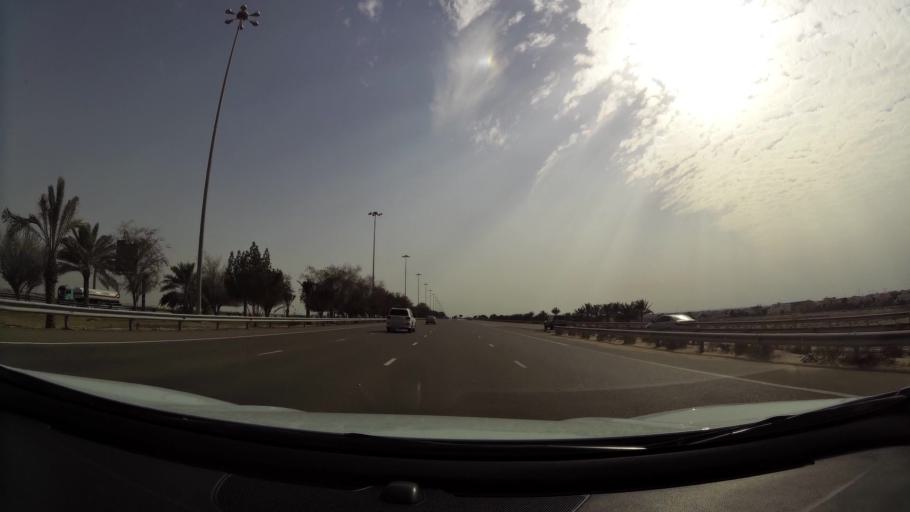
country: AE
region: Abu Dhabi
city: Abu Dhabi
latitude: 24.3951
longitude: 54.6662
